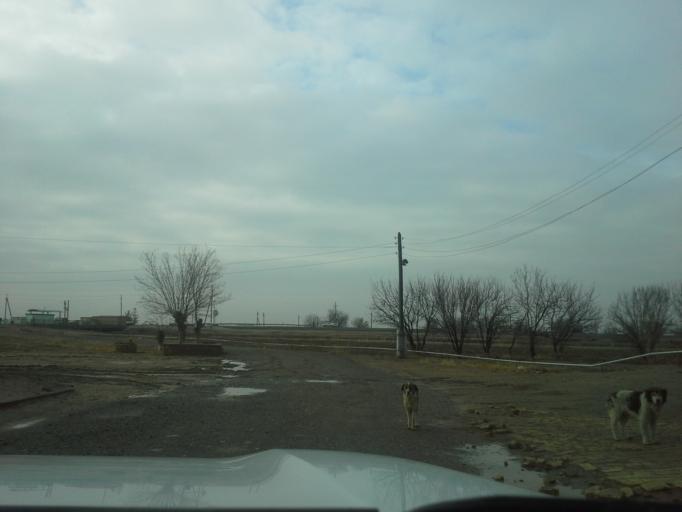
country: TM
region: Mary
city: Bayramaly
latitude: 37.4115
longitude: 62.1691
